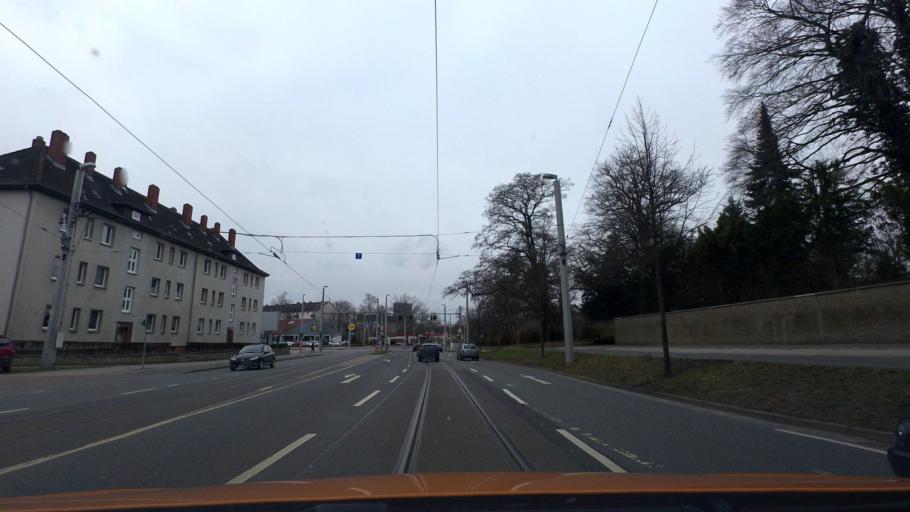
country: DE
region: Lower Saxony
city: Braunschweig
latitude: 52.2553
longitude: 10.5530
